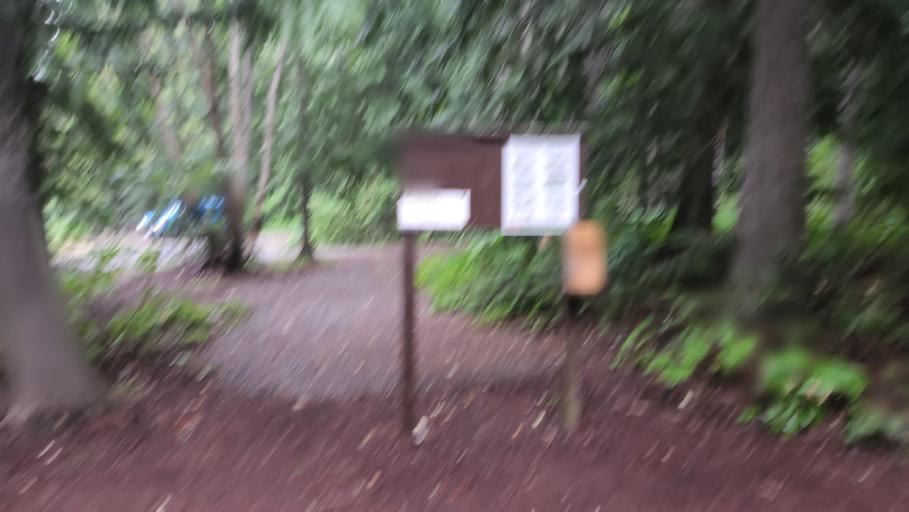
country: CA
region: British Columbia
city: Lillooet
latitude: 50.5359
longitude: -122.1353
